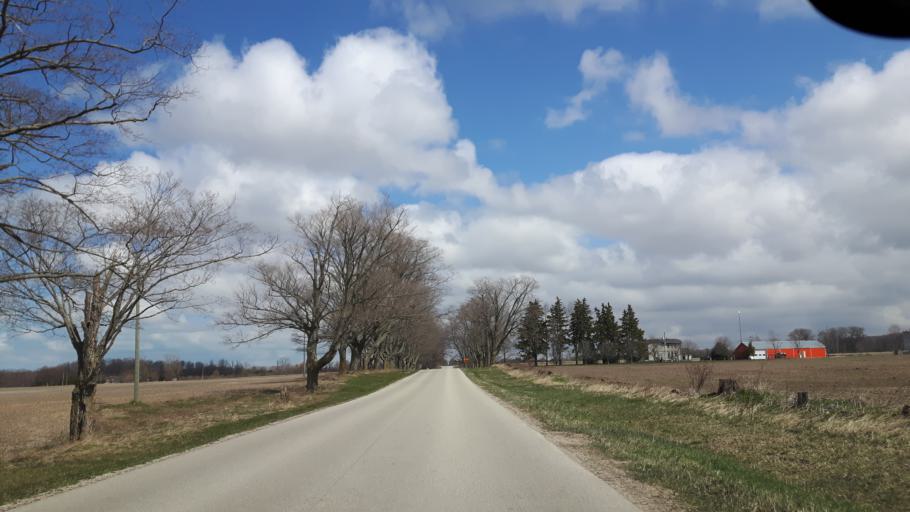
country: CA
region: Ontario
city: Goderich
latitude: 43.6381
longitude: -81.6846
